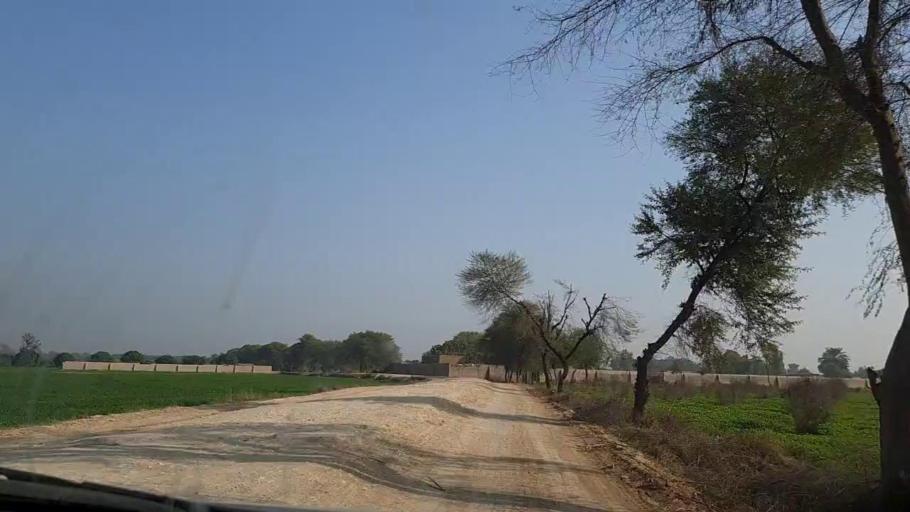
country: PK
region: Sindh
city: Moro
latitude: 26.8142
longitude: 67.9585
